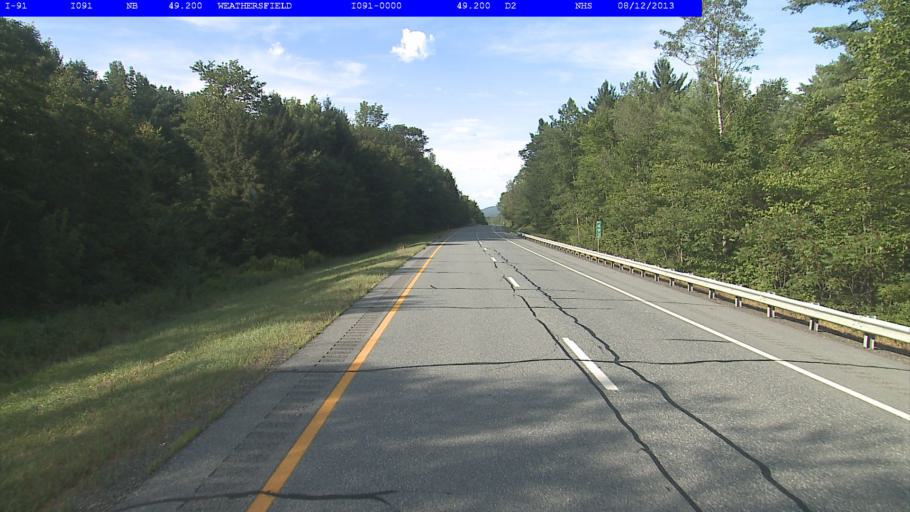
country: US
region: New Hampshire
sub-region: Sullivan County
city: Claremont
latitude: 43.3724
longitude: -72.4238
